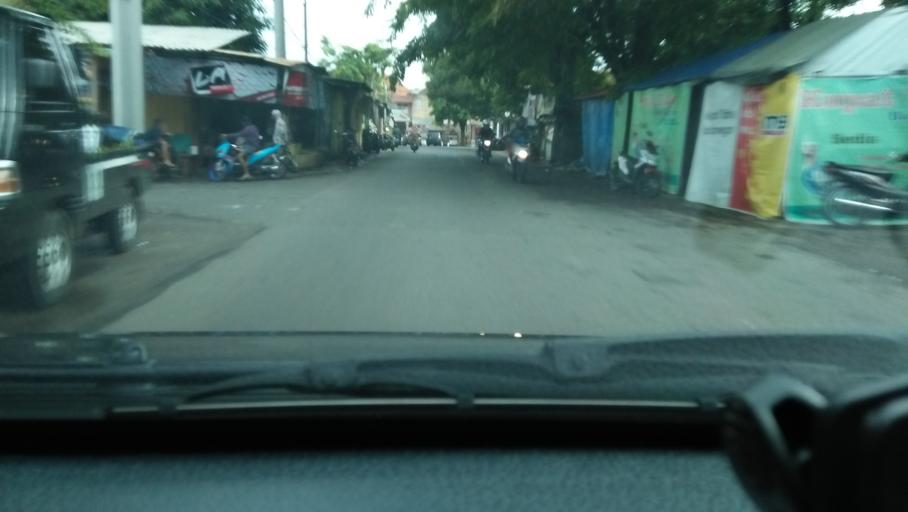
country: ID
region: Central Java
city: Semarang
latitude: -7.0647
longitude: 110.4167
